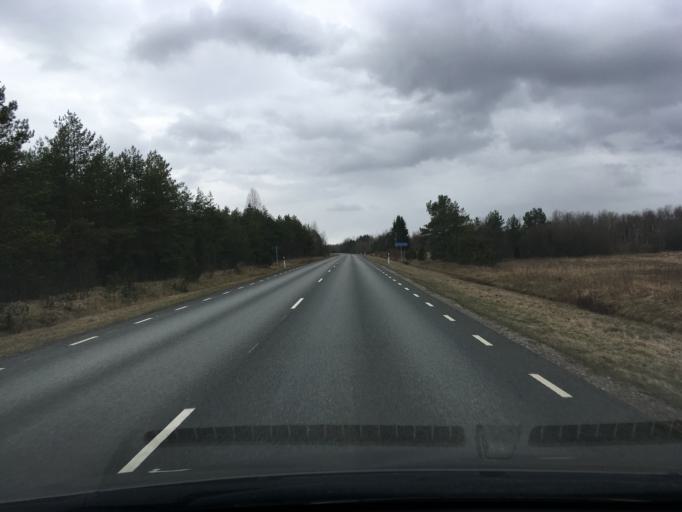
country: EE
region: Laeaene
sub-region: Lihula vald
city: Lihula
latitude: 58.6193
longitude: 23.9072
